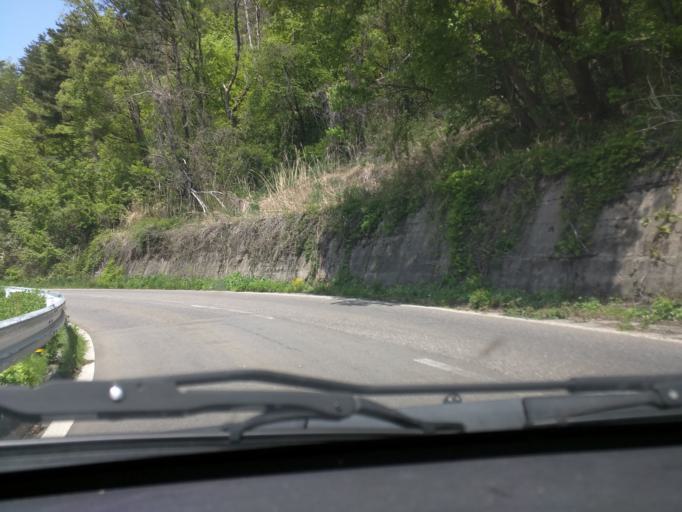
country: JP
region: Fukushima
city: Kitakata
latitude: 37.6395
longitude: 139.8091
